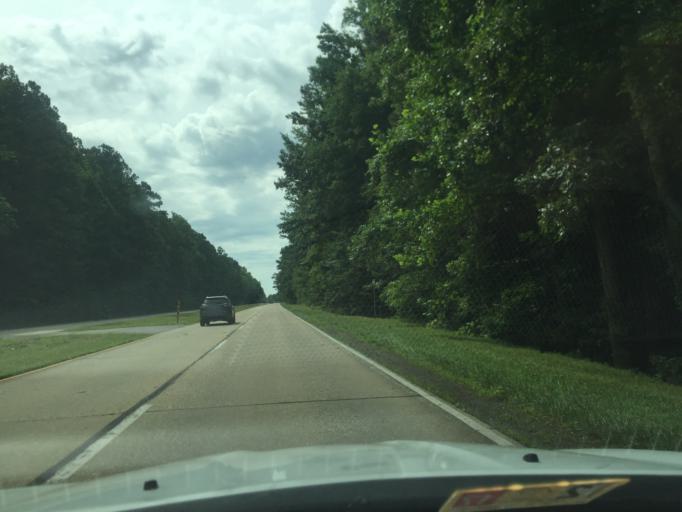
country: US
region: Virginia
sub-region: Charles City County
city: Charles City
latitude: 37.4667
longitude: -77.1089
